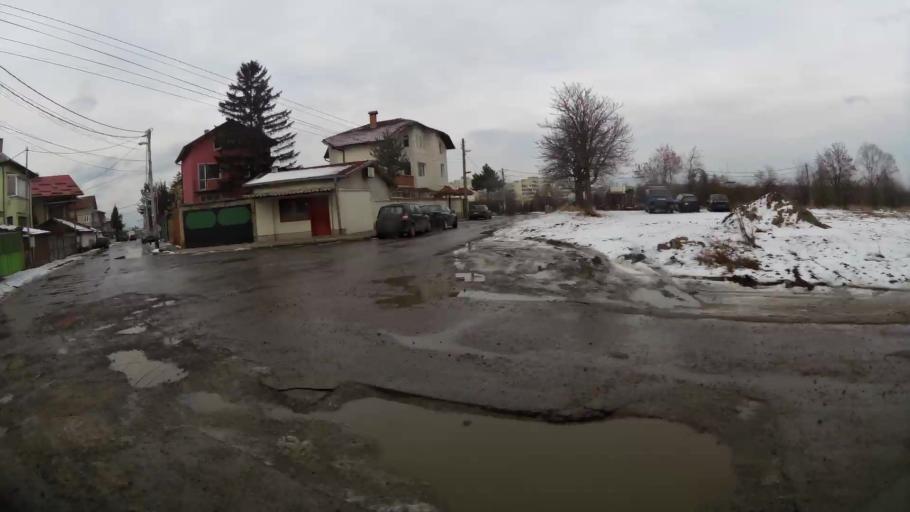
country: BG
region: Sofia-Capital
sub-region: Stolichna Obshtina
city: Sofia
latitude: 42.7194
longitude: 23.3460
